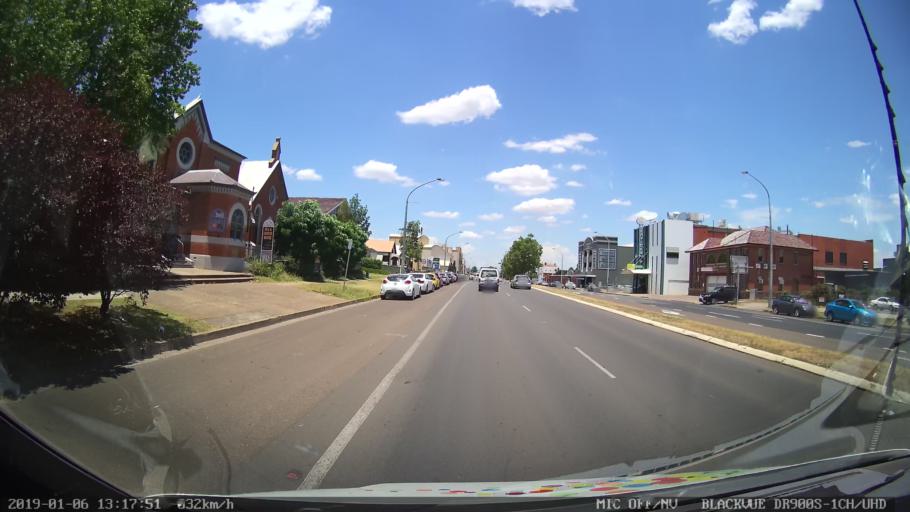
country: AU
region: New South Wales
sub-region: Tamworth Municipality
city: Tamworth
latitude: -31.0887
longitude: 150.9313
